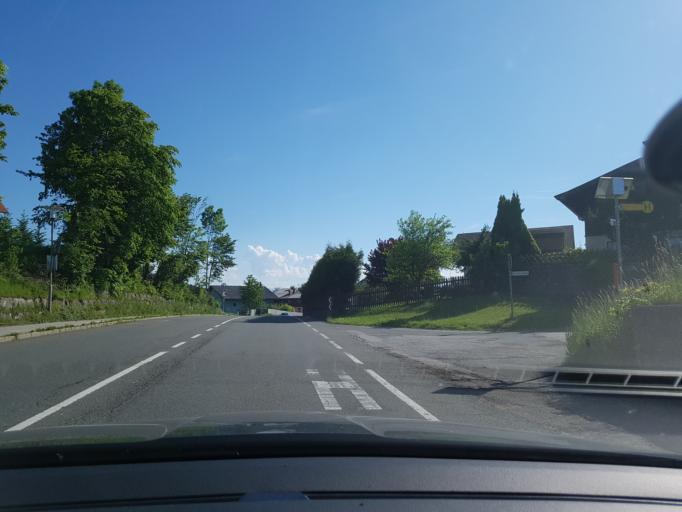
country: AT
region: Salzburg
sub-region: Politischer Bezirk Salzburg-Umgebung
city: Obertrum am See
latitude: 47.9387
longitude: 13.0862
